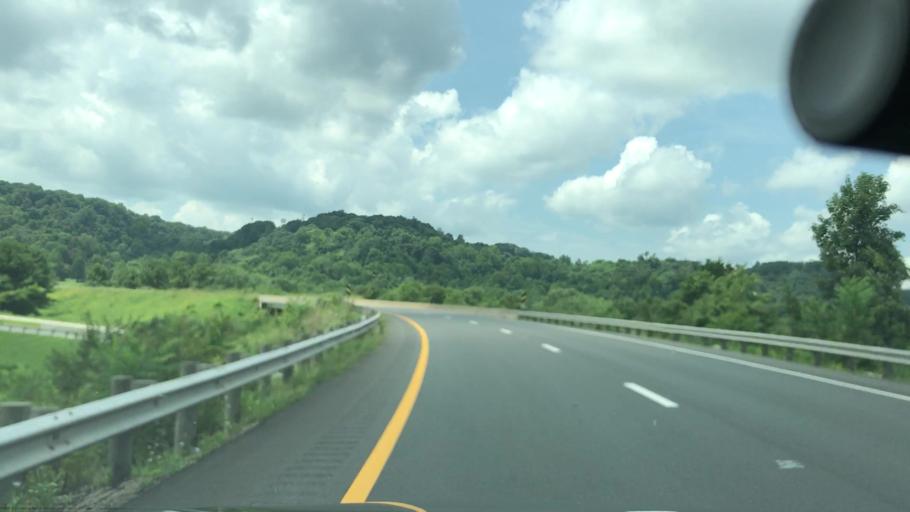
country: US
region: West Virginia
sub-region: Mason County
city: Point Pleasant
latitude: 38.8407
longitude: -82.1547
